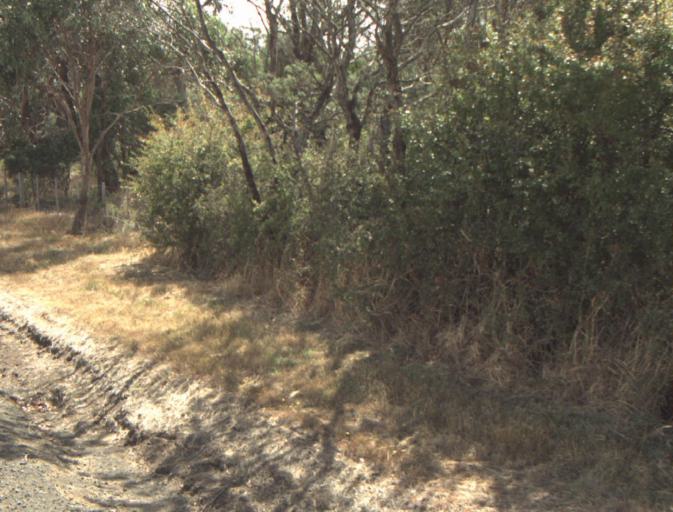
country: AU
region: Tasmania
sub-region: Northern Midlands
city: Evandale
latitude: -41.5153
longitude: 147.2929
